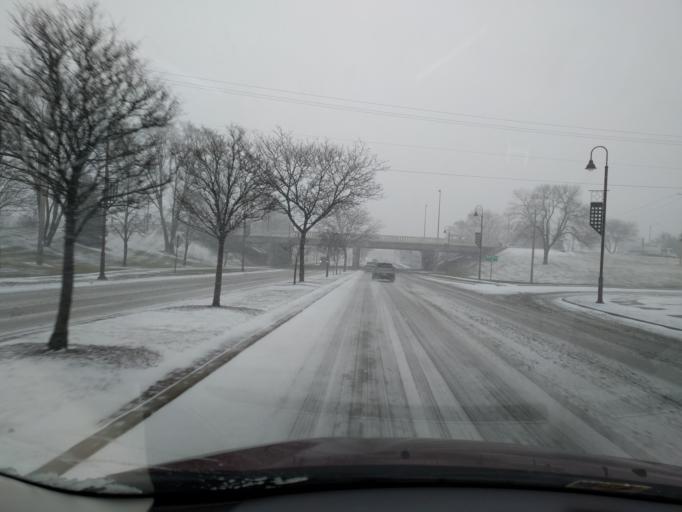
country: US
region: Wisconsin
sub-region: Milwaukee County
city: Glendale
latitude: 43.1189
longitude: -87.9359
